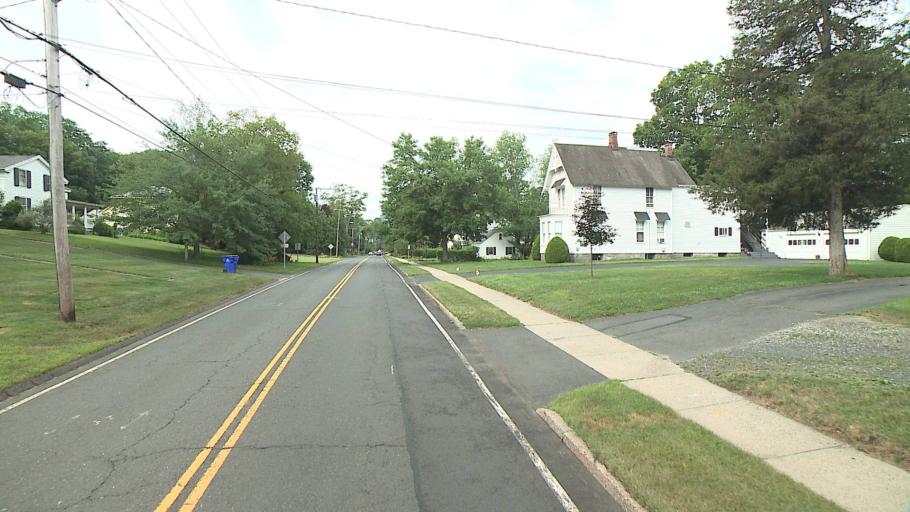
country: US
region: Connecticut
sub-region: Hartford County
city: Collinsville
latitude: 41.8166
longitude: -72.9179
